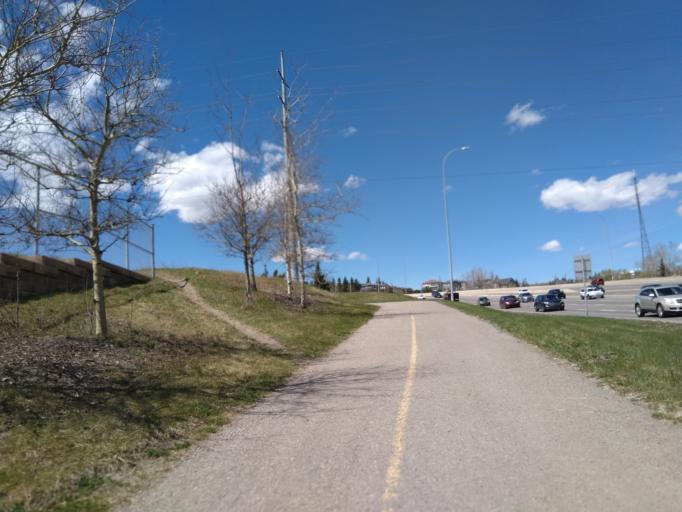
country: CA
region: Alberta
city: Calgary
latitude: 51.0524
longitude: -114.1647
